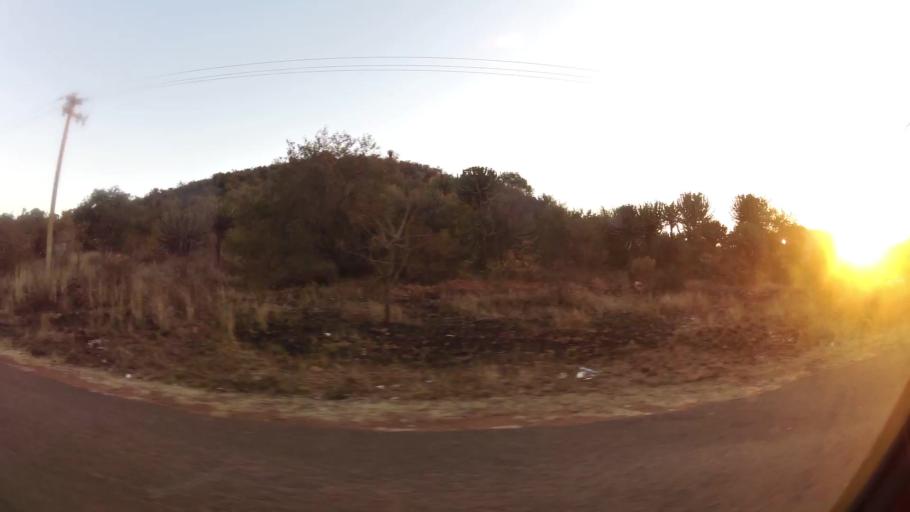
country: ZA
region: North-West
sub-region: Bojanala Platinum District Municipality
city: Rustenburg
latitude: -25.6210
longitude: 27.1954
